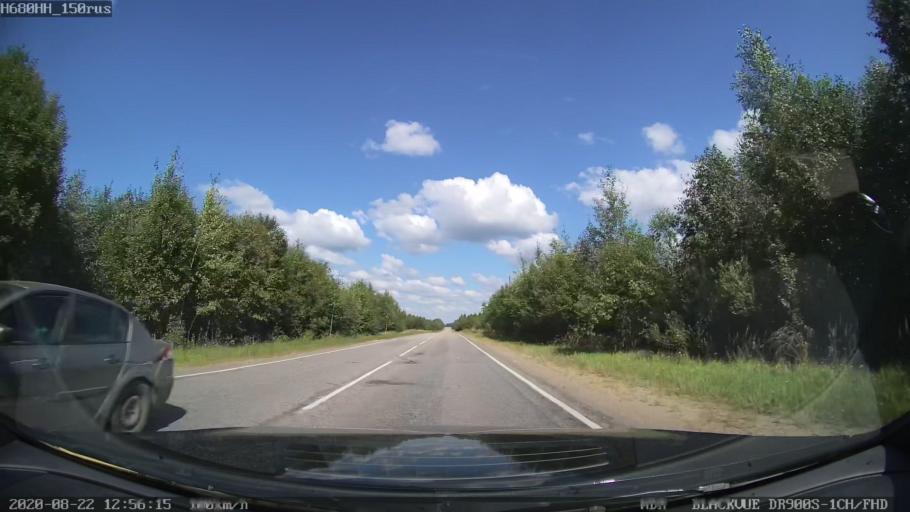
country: RU
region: Tverskaya
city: Rameshki
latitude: 57.5537
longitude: 36.3143
